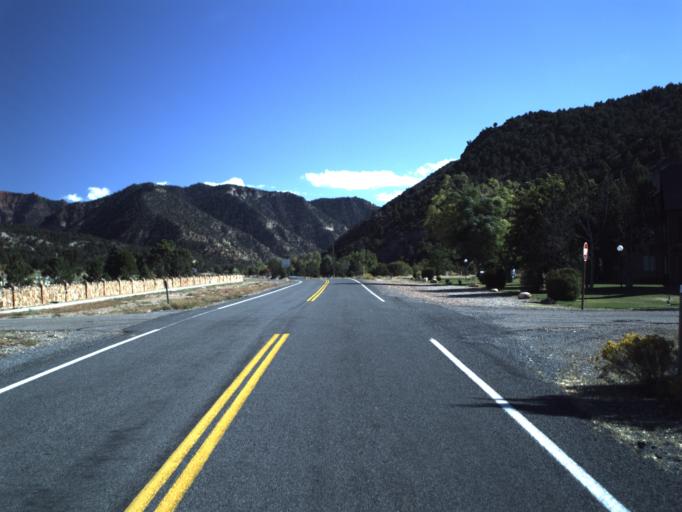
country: US
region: Utah
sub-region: Iron County
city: Parowan
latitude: 37.8379
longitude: -112.8195
